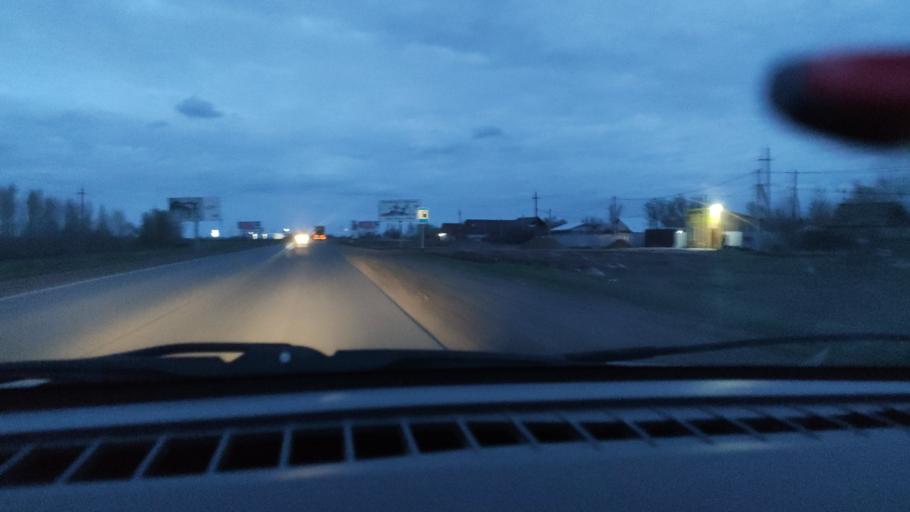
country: RU
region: Orenburg
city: Tatarskaya Kargala
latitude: 51.9019
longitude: 55.1678
